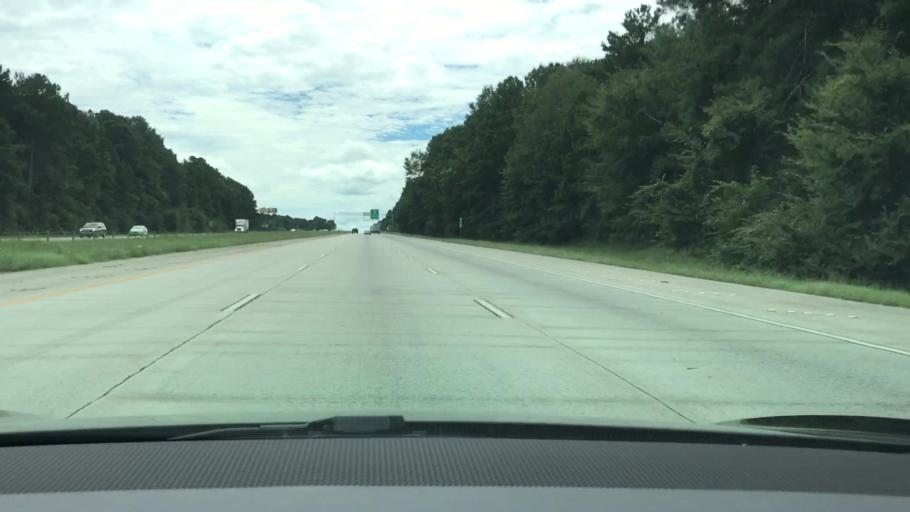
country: US
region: Georgia
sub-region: Coweta County
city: Grantville
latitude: 33.2536
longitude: -84.8061
